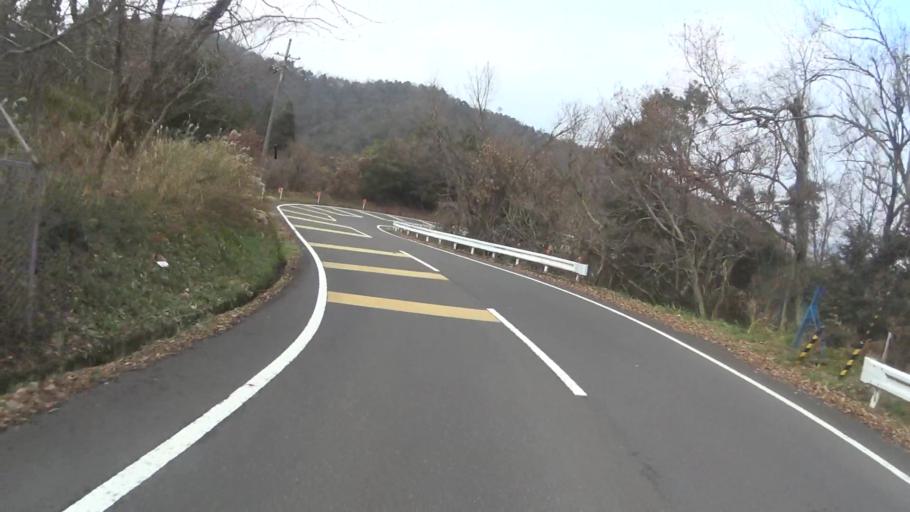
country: JP
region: Kyoto
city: Maizuru
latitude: 35.4443
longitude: 135.3938
